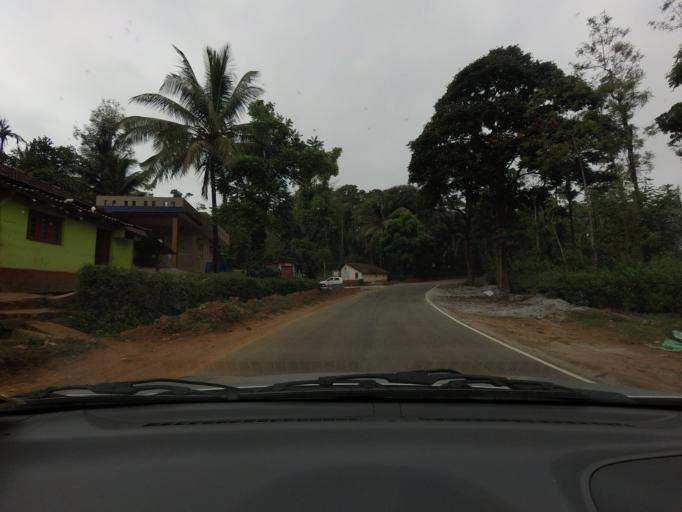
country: IN
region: Karnataka
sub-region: Hassan
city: Sakleshpur
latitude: 12.9434
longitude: 75.7523
